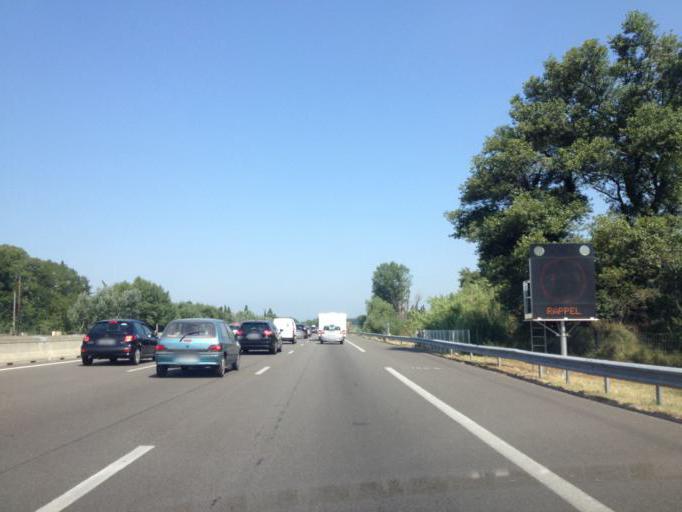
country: FR
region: Provence-Alpes-Cote d'Azur
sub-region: Departement du Vaucluse
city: Mondragon
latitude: 44.2198
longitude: 4.7181
